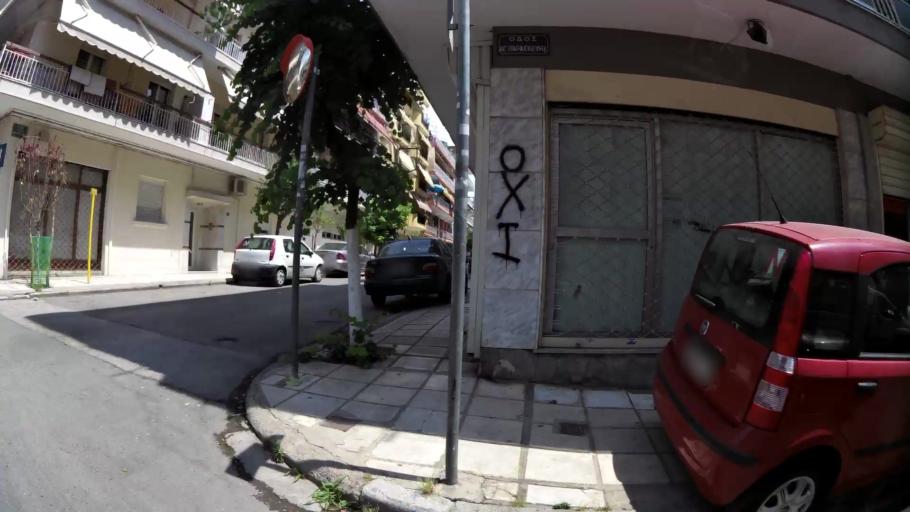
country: GR
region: Central Macedonia
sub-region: Nomos Thessalonikis
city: Ampelokipoi
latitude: 40.6513
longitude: 22.9305
